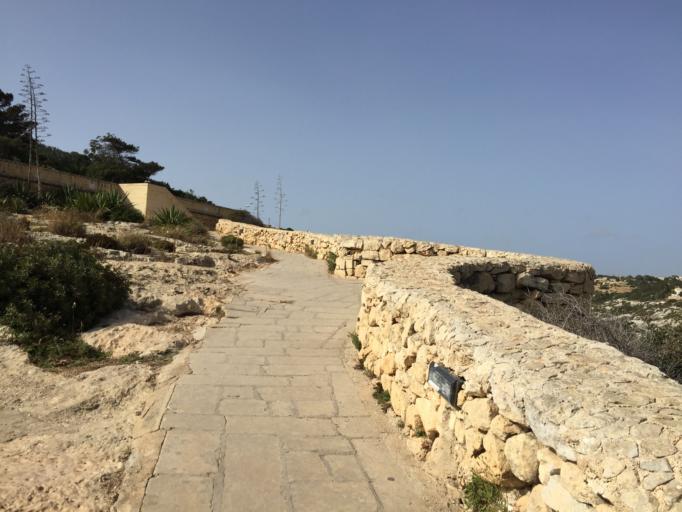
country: MT
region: Il-Qrendi
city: Qrendi
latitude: 35.8221
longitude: 14.4576
